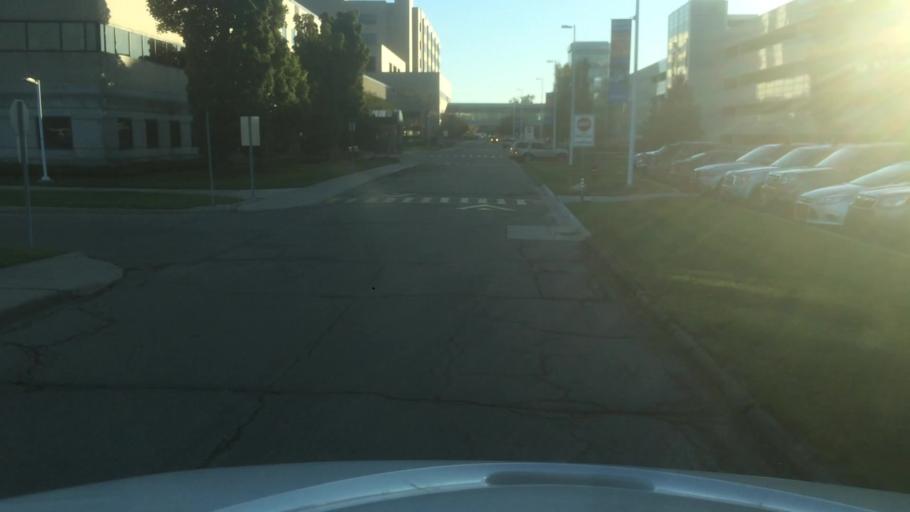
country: US
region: Michigan
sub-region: Oakland County
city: Berkley
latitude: 42.5134
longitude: -83.1942
